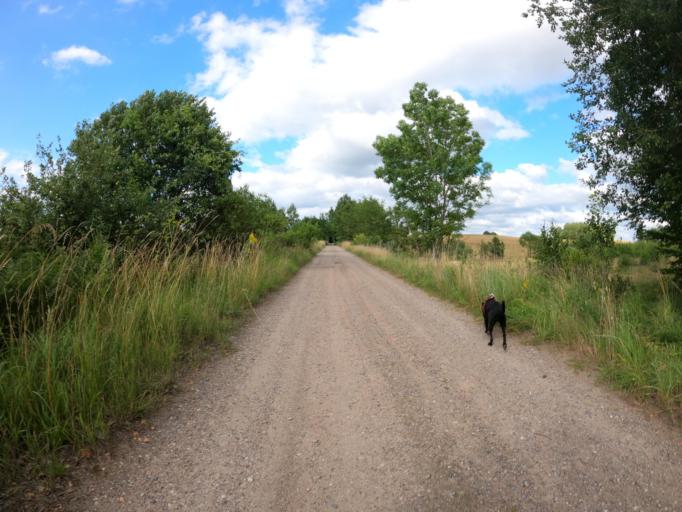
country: PL
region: West Pomeranian Voivodeship
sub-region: Powiat szczecinecki
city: Grzmiaca
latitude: 53.8784
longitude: 16.4723
